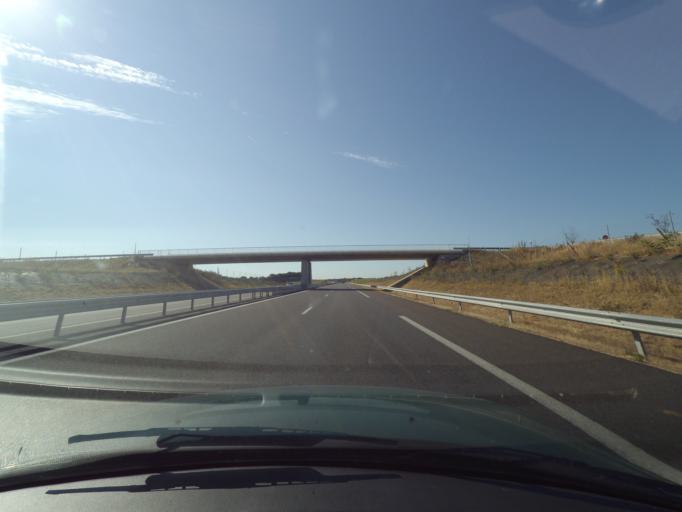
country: FR
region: Poitou-Charentes
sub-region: Departement de la Vienne
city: Terce
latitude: 46.4732
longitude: 0.5416
